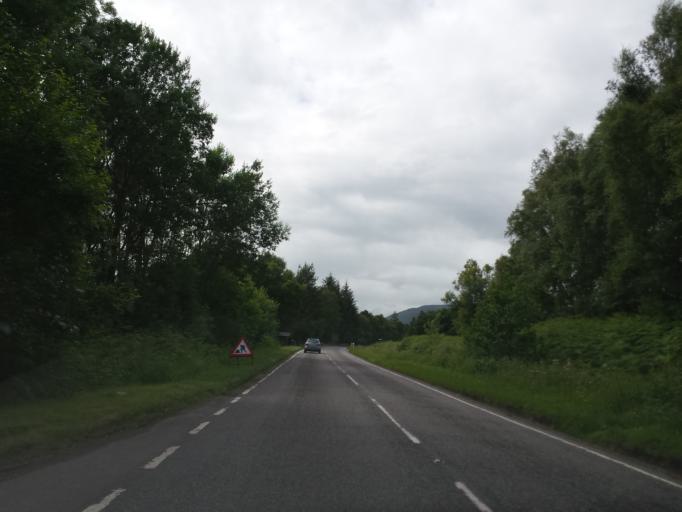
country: GB
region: Scotland
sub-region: Highland
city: Fort William
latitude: 56.8536
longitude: -5.1828
